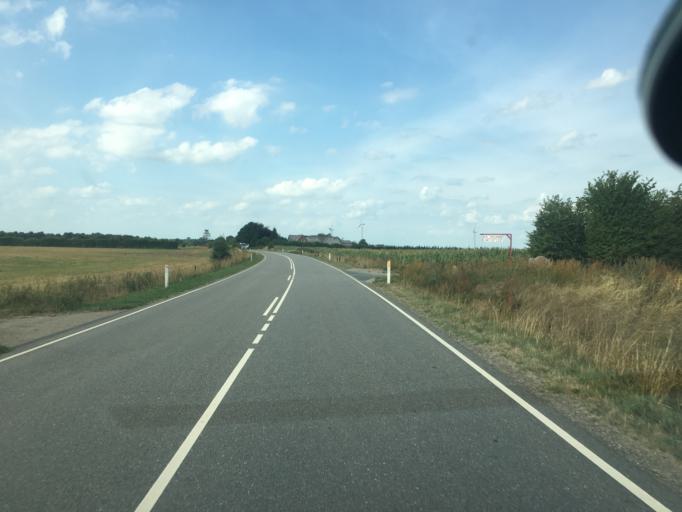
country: DK
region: South Denmark
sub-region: Aabenraa Kommune
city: Krusa
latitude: 54.9398
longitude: 9.3531
